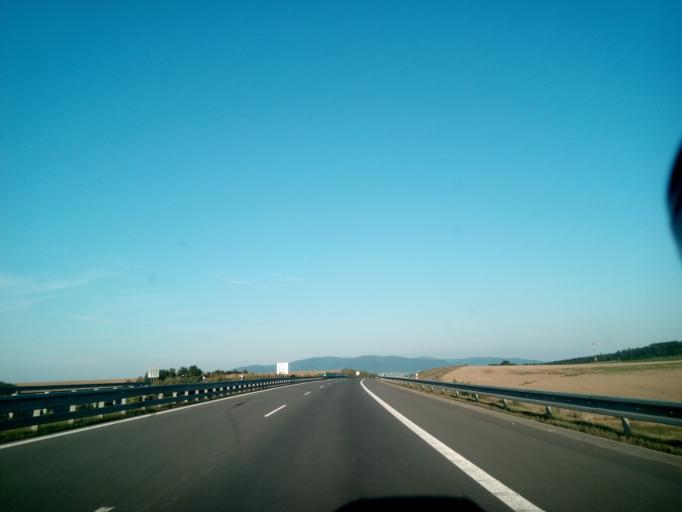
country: SK
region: Presovsky
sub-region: Okres Presov
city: Presov
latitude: 49.0076
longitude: 21.1386
